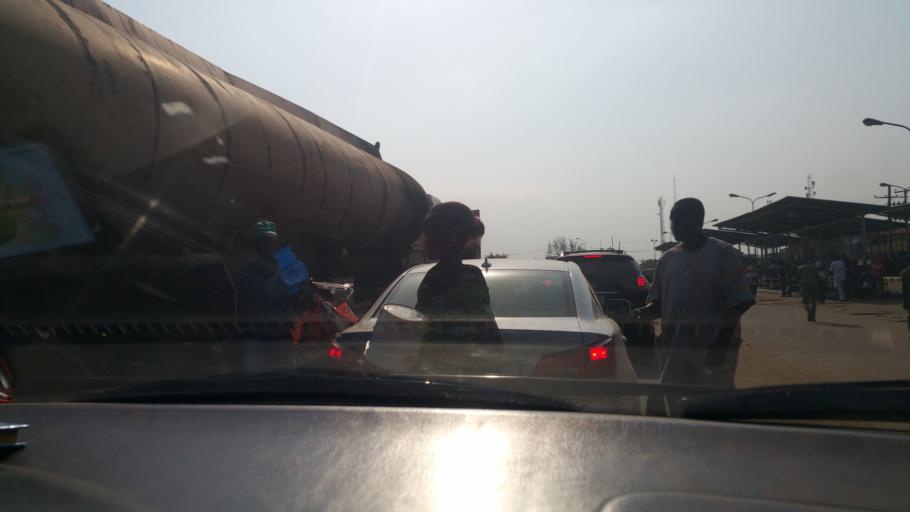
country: NG
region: Lagos
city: Ikotun
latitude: 6.5518
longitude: 3.2416
